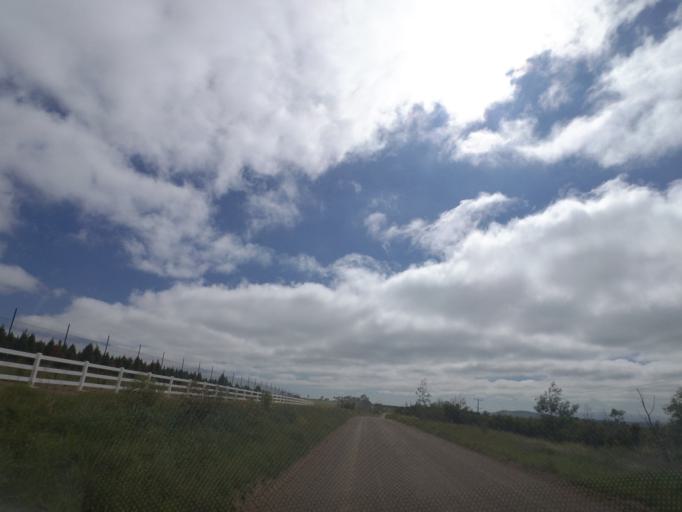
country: AU
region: Victoria
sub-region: Hume
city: Craigieburn
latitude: -37.4961
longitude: 144.9063
